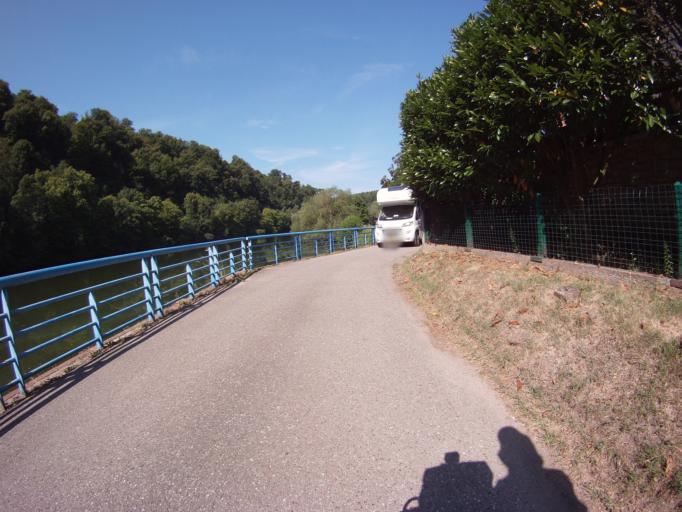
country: FR
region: Lorraine
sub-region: Departement de Meurthe-et-Moselle
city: Liverdun
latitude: 48.7452
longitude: 6.0634
